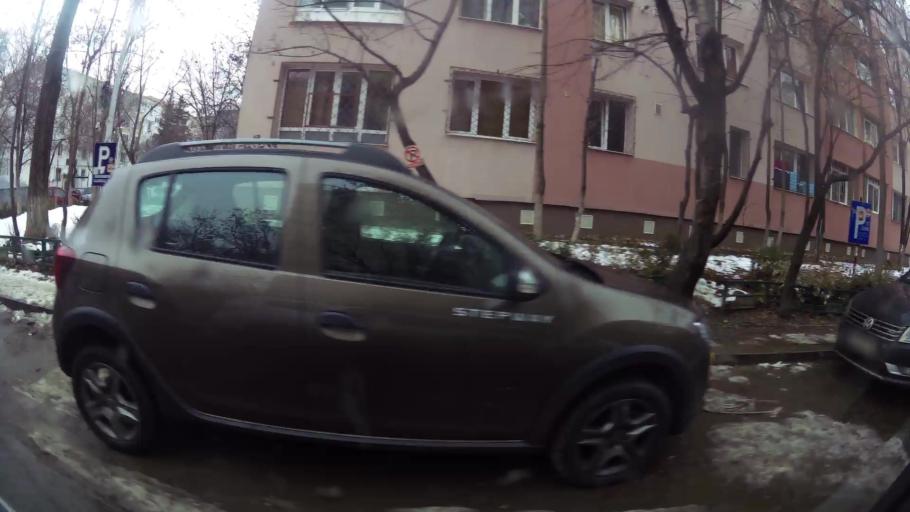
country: RO
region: Ilfov
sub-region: Comuna Chiajna
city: Rosu
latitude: 44.4162
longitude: 26.0334
